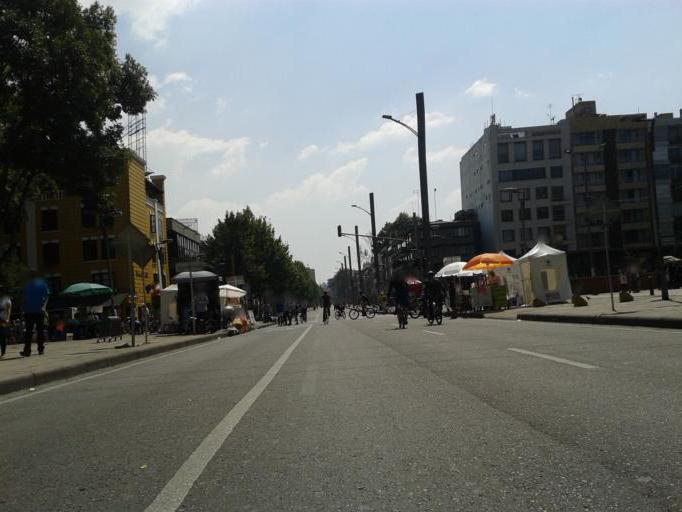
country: CO
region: Bogota D.C.
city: Barrio San Luis
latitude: 4.6732
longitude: -74.0538
